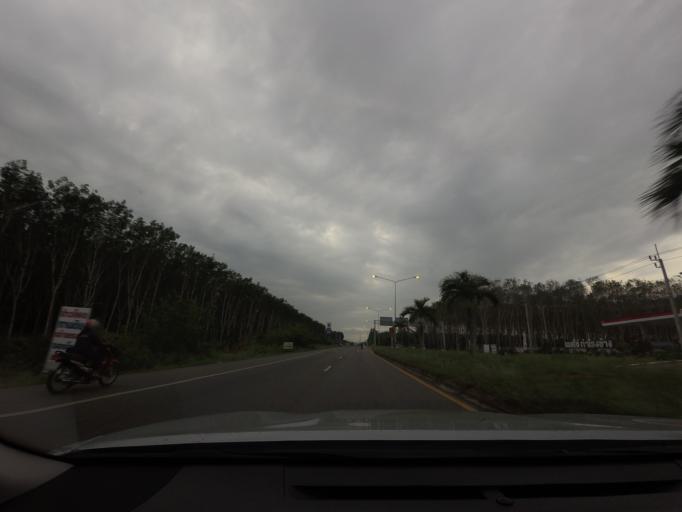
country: TH
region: Surat Thani
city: Phunphin
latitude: 9.0447
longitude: 99.1538
